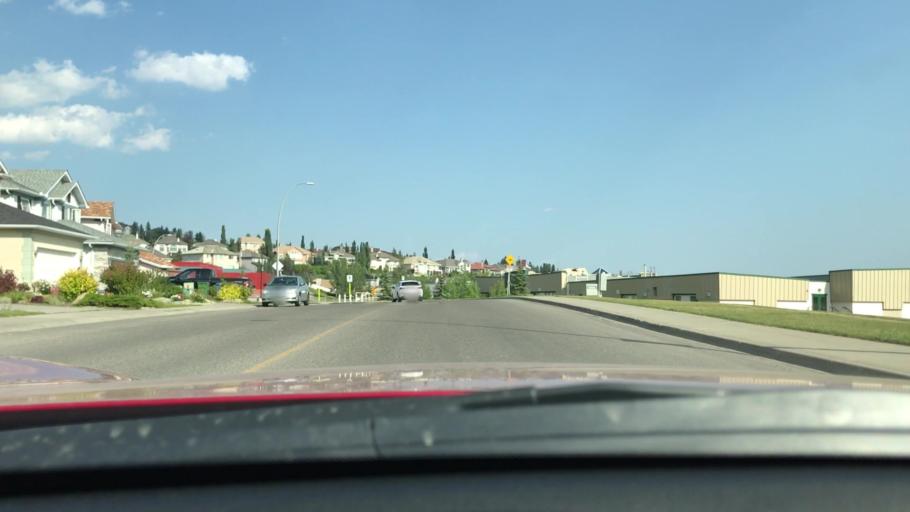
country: CA
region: Alberta
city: Calgary
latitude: 51.0242
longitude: -114.1832
